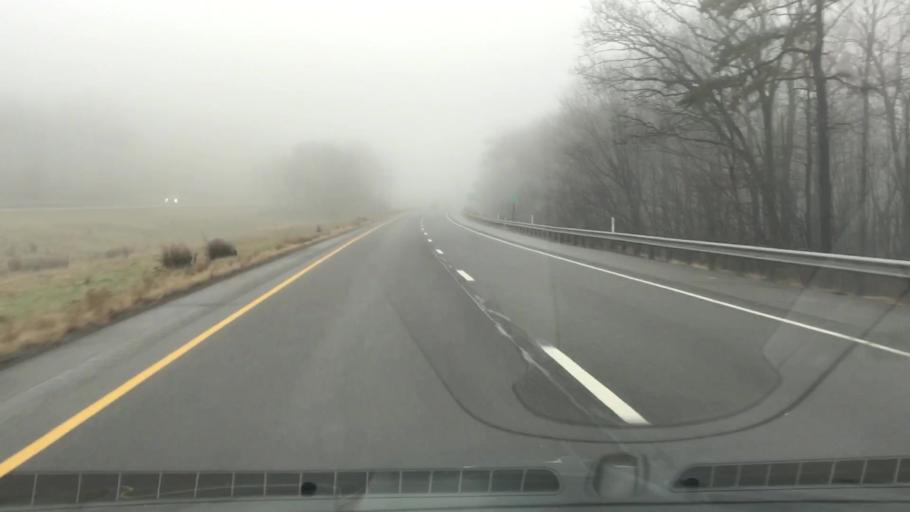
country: US
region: Pennsylvania
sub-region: Wayne County
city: Hawley
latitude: 41.3600
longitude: -75.1707
